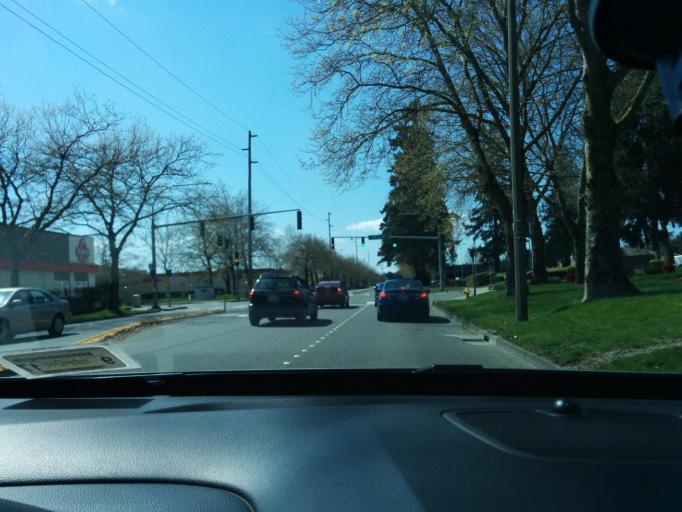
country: US
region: Washington
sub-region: King County
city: Redmond
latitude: 47.6316
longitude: -122.1386
